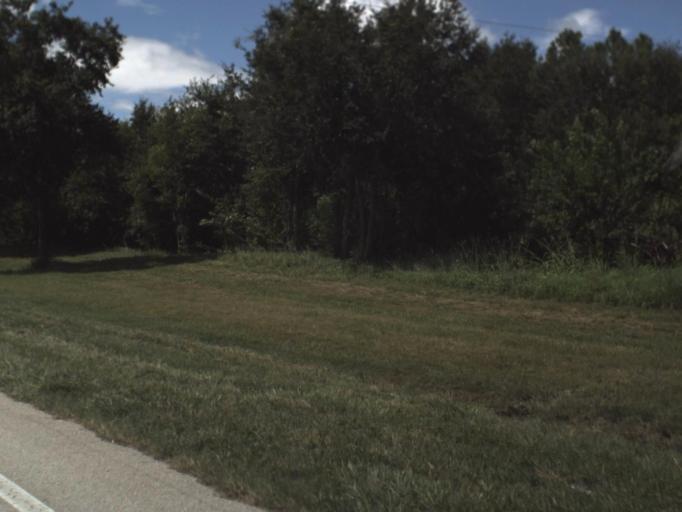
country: US
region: Florida
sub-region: Polk County
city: Mulberry
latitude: 27.8477
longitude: -81.9785
